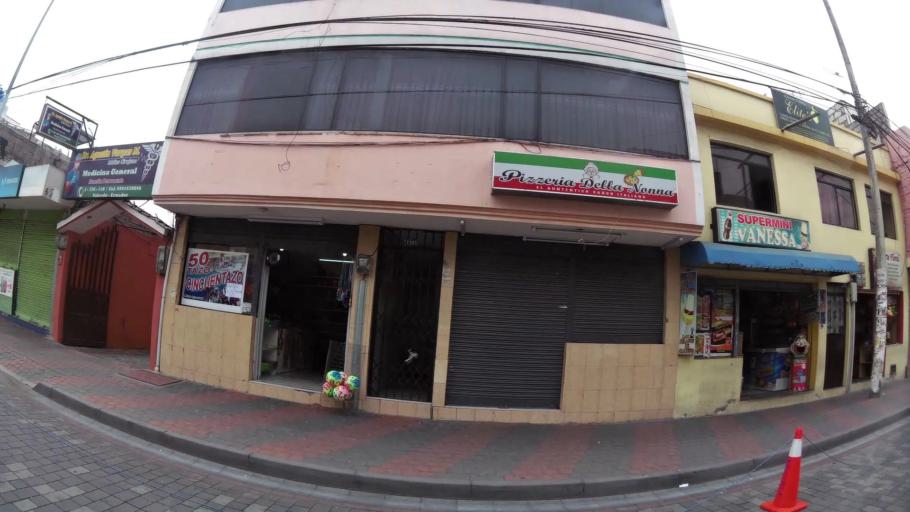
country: EC
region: Cotopaxi
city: San Miguel de Salcedo
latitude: -1.0419
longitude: -78.5907
